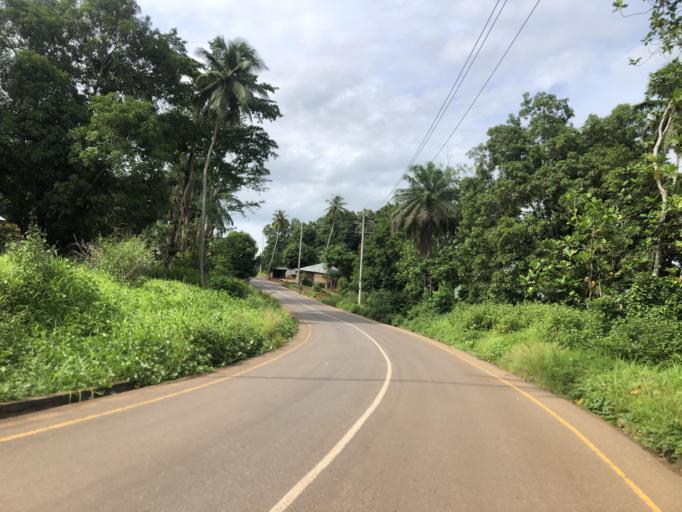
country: SL
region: Northern Province
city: Port Loko
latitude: 8.7569
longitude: -12.7875
